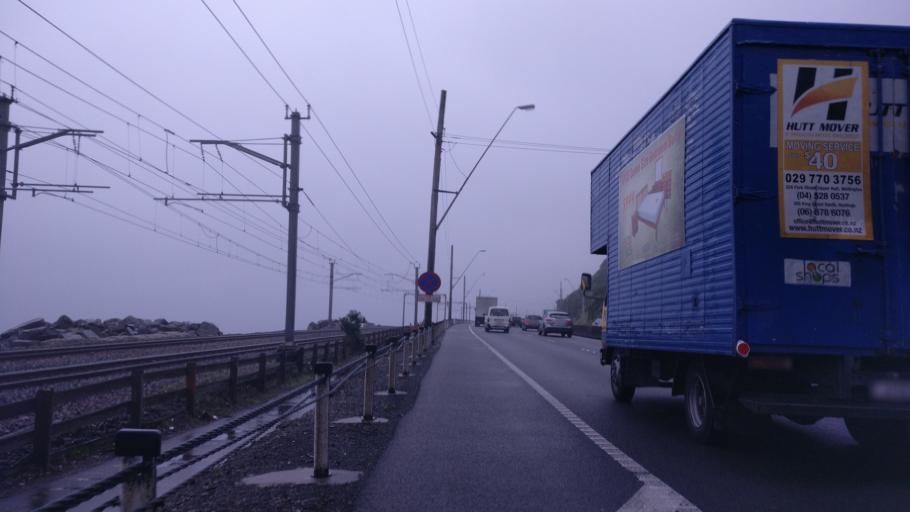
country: NZ
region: Wellington
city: Petone
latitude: -41.2335
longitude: 174.8363
